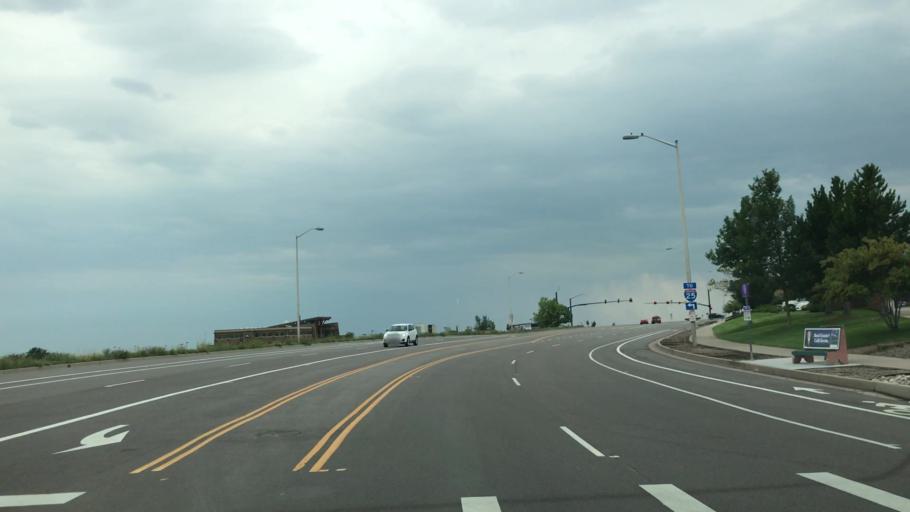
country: US
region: Colorado
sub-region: El Paso County
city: Colorado Springs
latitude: 38.8784
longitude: -104.8473
